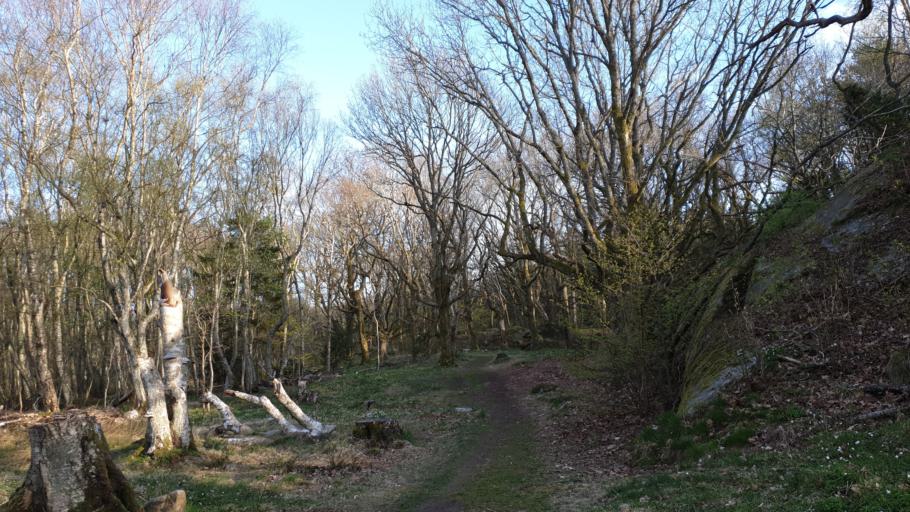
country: SE
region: Vaestra Goetaland
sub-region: Goteborg
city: Billdal
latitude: 57.5947
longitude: 11.9110
